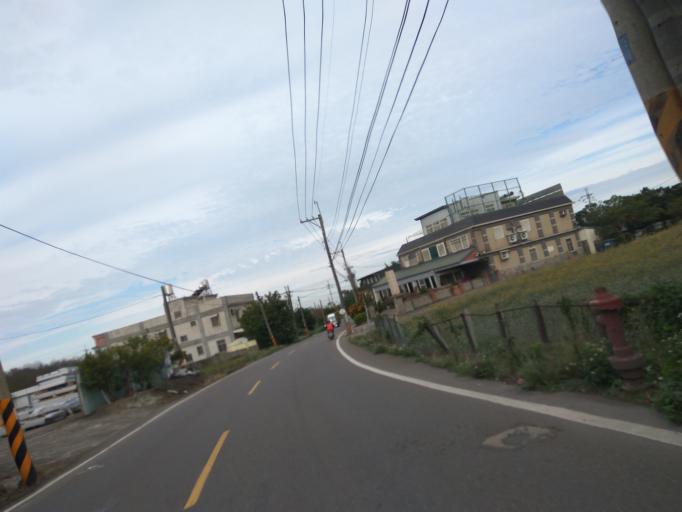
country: TW
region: Taiwan
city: Daxi
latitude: 24.9463
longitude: 121.1454
